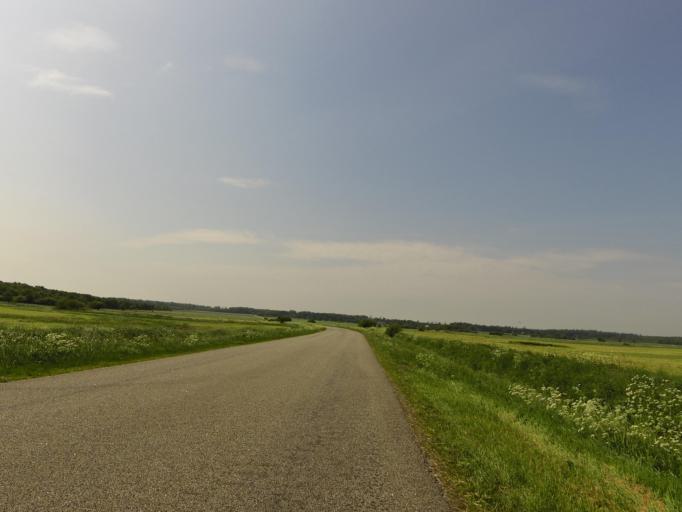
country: DK
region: South Denmark
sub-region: Tonder Kommune
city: Toftlund
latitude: 55.1924
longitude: 8.9904
